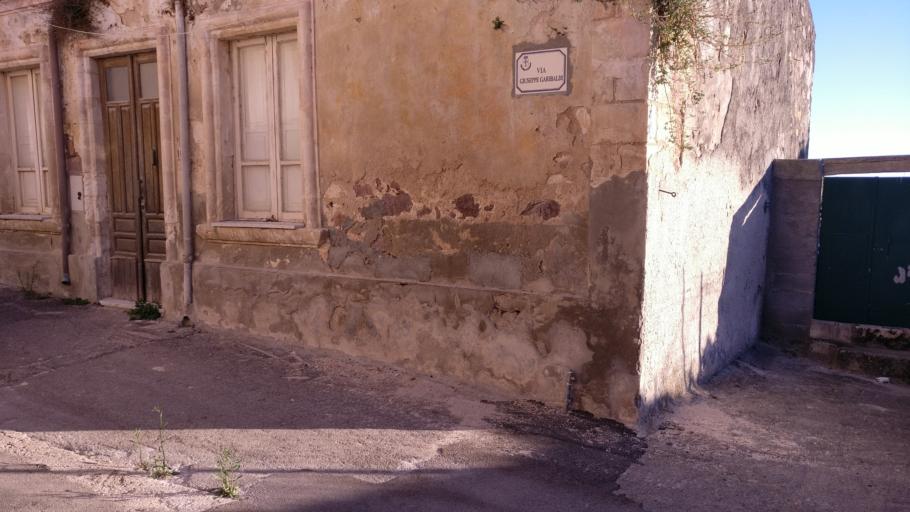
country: IT
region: Sardinia
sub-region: Provincia di Sassari
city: Uri
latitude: 40.6346
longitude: 8.4897
